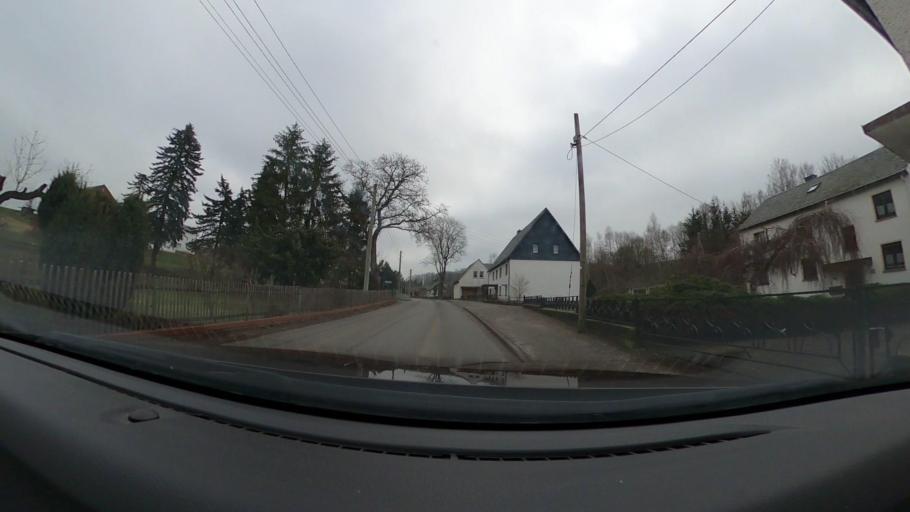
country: DE
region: Saxony
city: Oberschona
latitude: 50.8941
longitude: 13.2589
